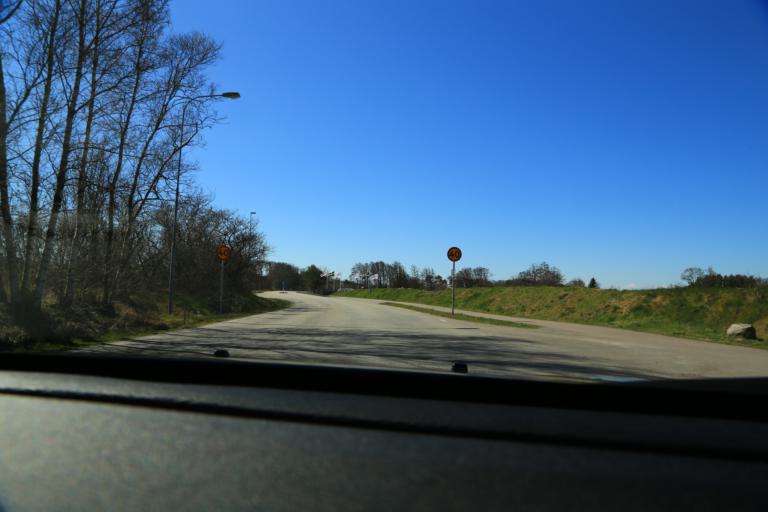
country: SE
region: Halland
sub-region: Varbergs Kommun
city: Traslovslage
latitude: 57.0719
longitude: 12.2875
